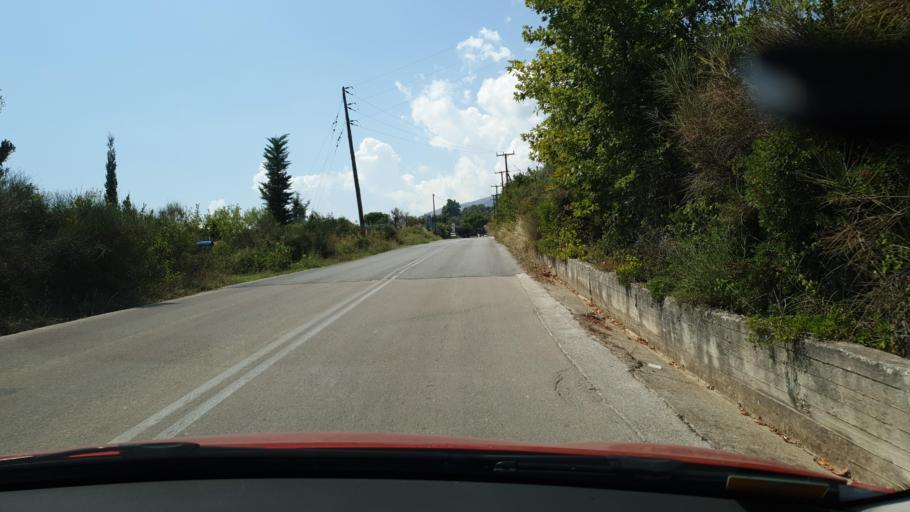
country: GR
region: Central Greece
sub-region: Nomos Evvoias
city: Oxilithos
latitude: 38.5922
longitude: 24.0724
